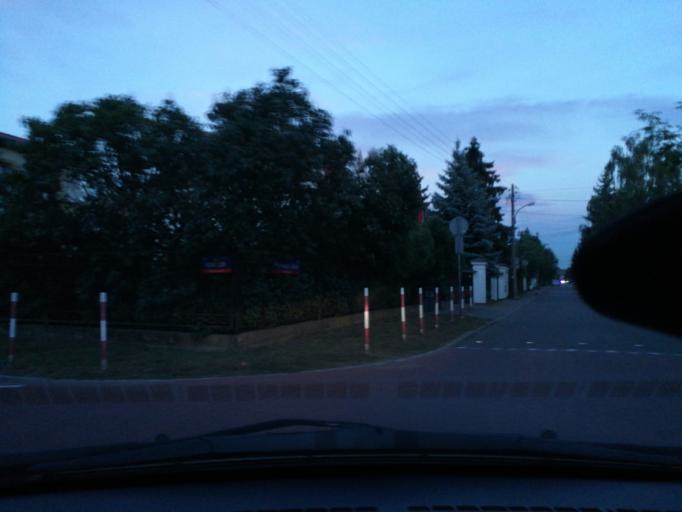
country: PL
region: Masovian Voivodeship
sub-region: Warszawa
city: Wilanow
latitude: 52.1747
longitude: 21.0733
